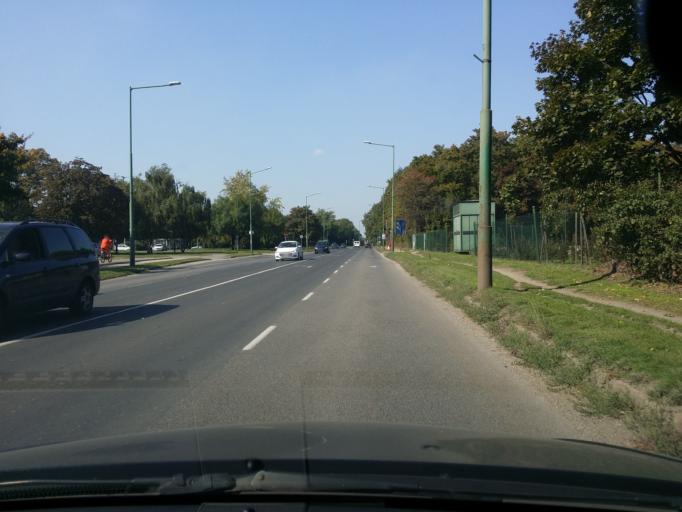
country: HU
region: Fejer
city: Dunaujvaros
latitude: 46.9509
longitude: 18.9497
